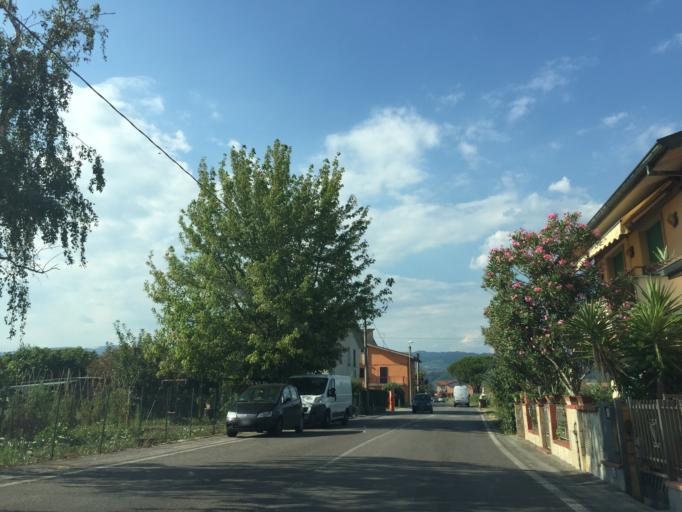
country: IT
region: Tuscany
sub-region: Provincia di Pistoia
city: Monsummano Terme
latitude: 43.8649
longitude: 10.7981
